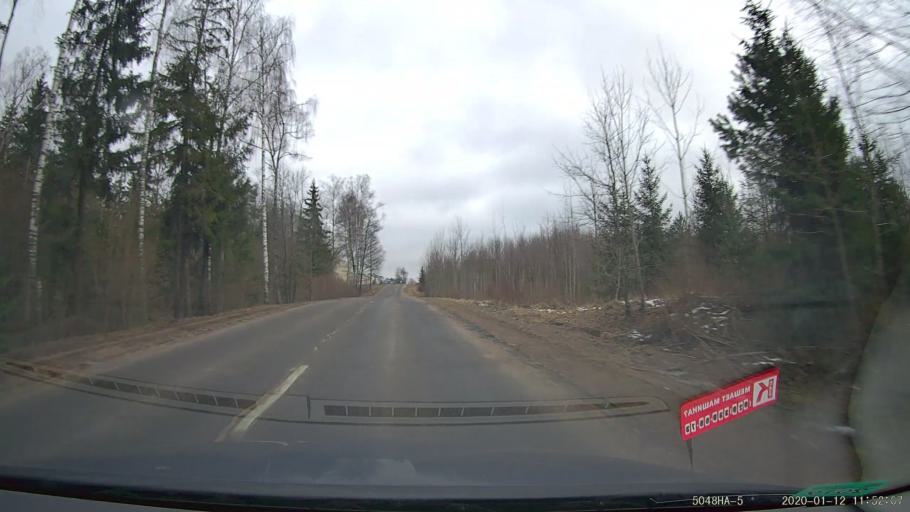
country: BY
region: Minsk
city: Rakaw
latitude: 53.9653
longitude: 27.1217
